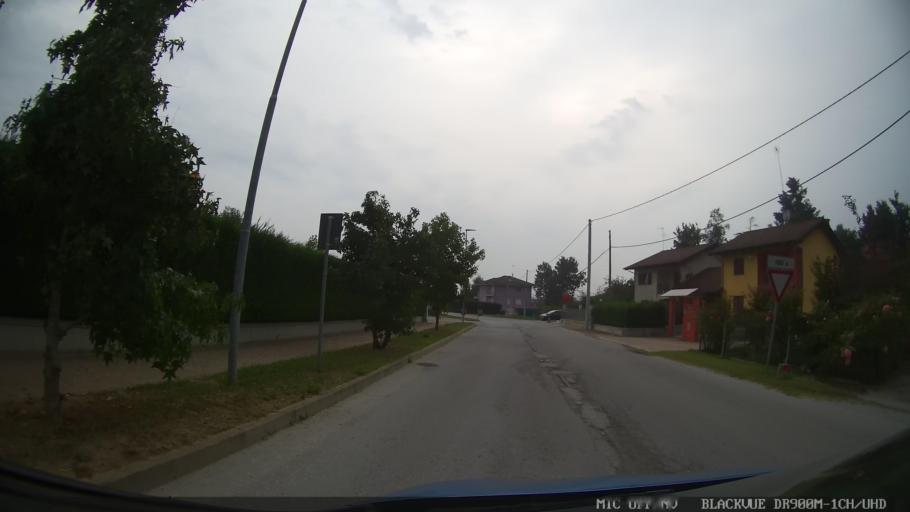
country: IT
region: Piedmont
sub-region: Provincia di Cuneo
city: Fossano
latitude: 44.5730
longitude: 7.7453
